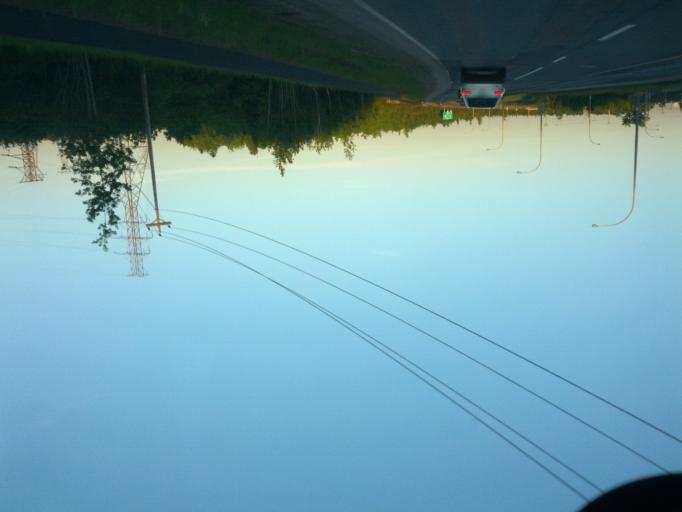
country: CA
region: New Brunswick
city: Moncton
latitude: 46.0957
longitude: -64.8450
